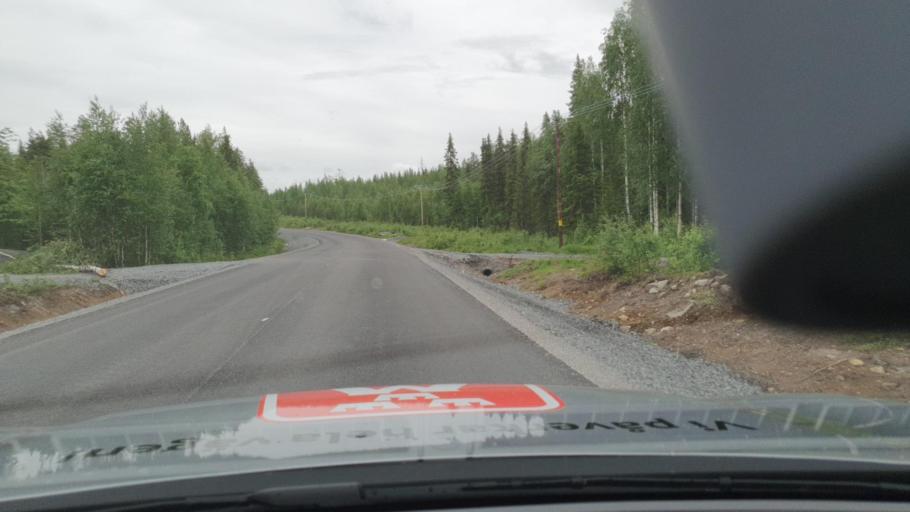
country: SE
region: Norrbotten
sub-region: Overtornea Kommun
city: OEvertornea
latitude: 66.6295
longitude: 23.2690
